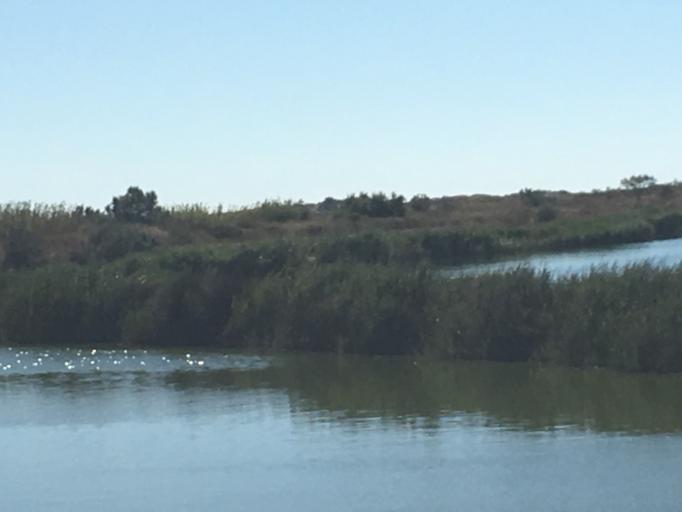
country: FR
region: Provence-Alpes-Cote d'Azur
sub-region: Departement des Bouches-du-Rhone
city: Saintes-Maries-de-la-Mer
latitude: 43.4624
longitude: 4.4562
